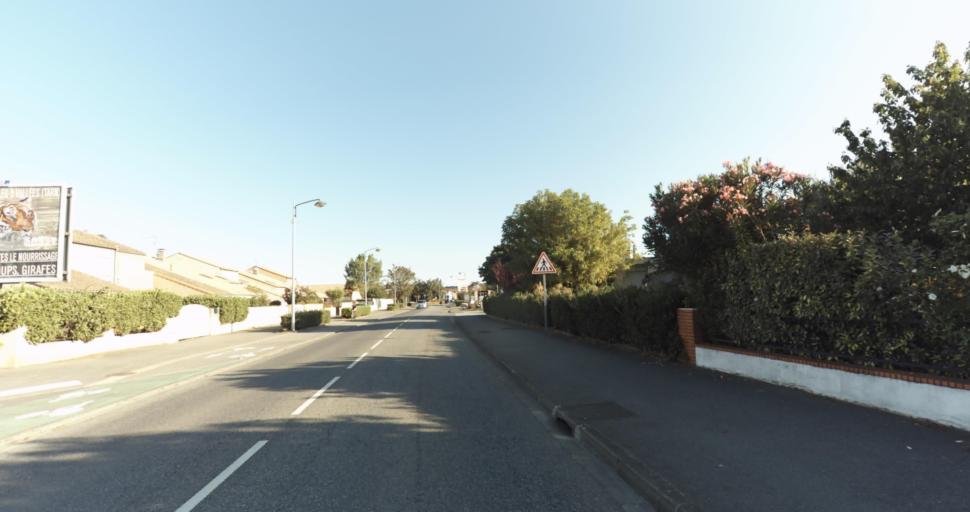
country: FR
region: Midi-Pyrenees
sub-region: Departement de la Haute-Garonne
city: L'Union
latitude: 43.6539
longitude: 1.4708
